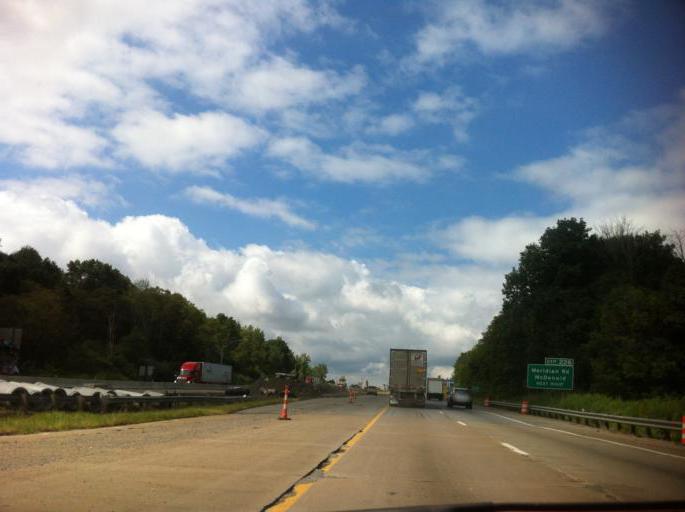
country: US
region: Ohio
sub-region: Trumbull County
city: Girard
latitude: 41.1463
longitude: -80.7115
